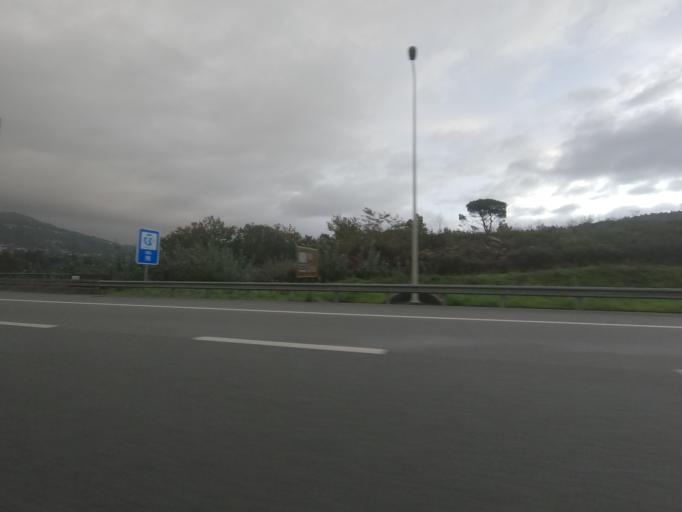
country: PT
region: Viana do Castelo
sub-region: Ponte de Lima
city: Ponte de Lima
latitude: 41.7731
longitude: -8.5583
